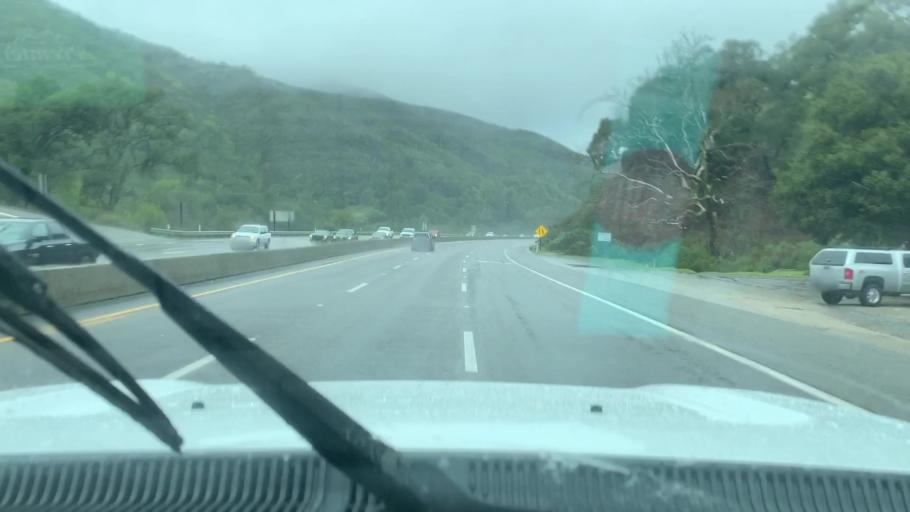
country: US
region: California
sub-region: San Luis Obispo County
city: Santa Margarita
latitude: 35.3489
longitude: -120.6332
